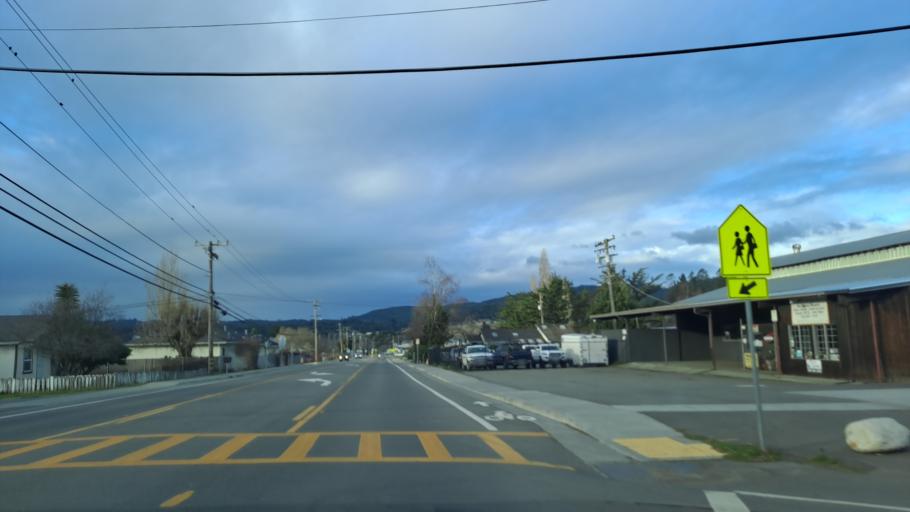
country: US
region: California
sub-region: Humboldt County
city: Fortuna
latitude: 40.5792
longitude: -124.1300
